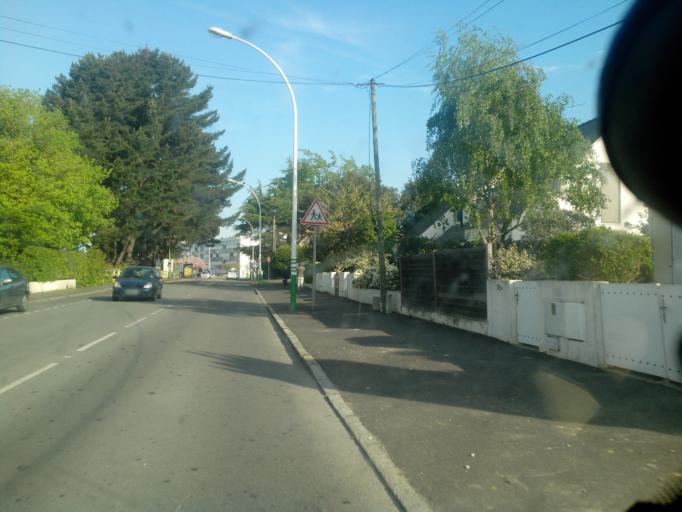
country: FR
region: Pays de la Loire
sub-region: Departement de la Loire-Atlantique
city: Orvault
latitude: 47.2410
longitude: -1.6065
